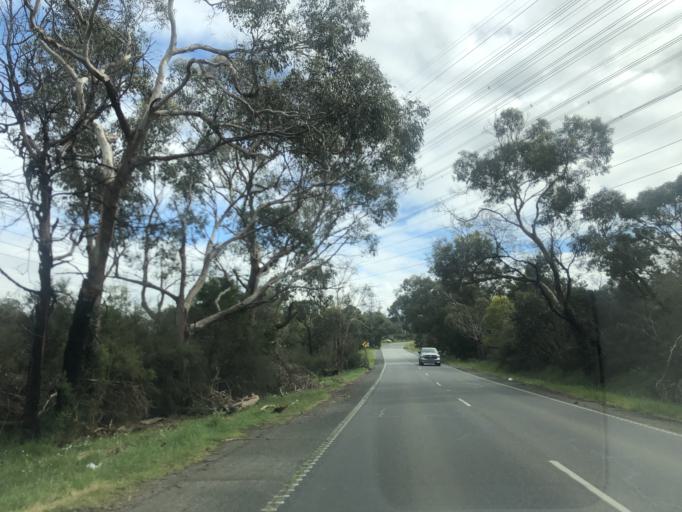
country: AU
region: Victoria
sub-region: Knox
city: Rowville
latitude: -37.9456
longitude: 145.2446
